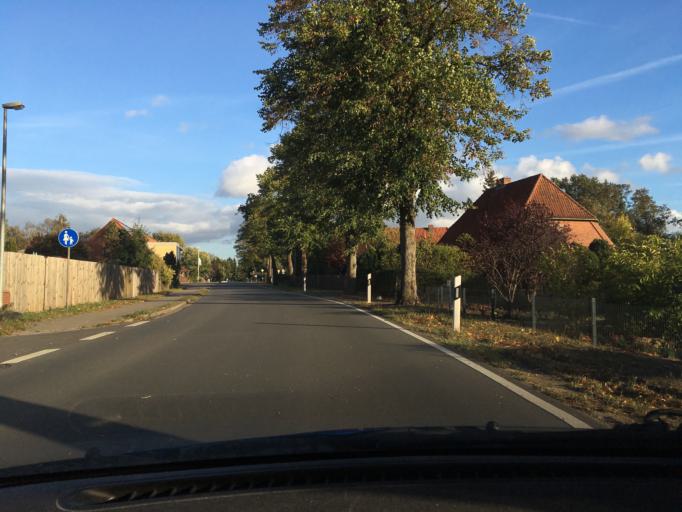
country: DE
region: Lower Saxony
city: Hittbergen
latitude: 53.3477
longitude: 10.5700
